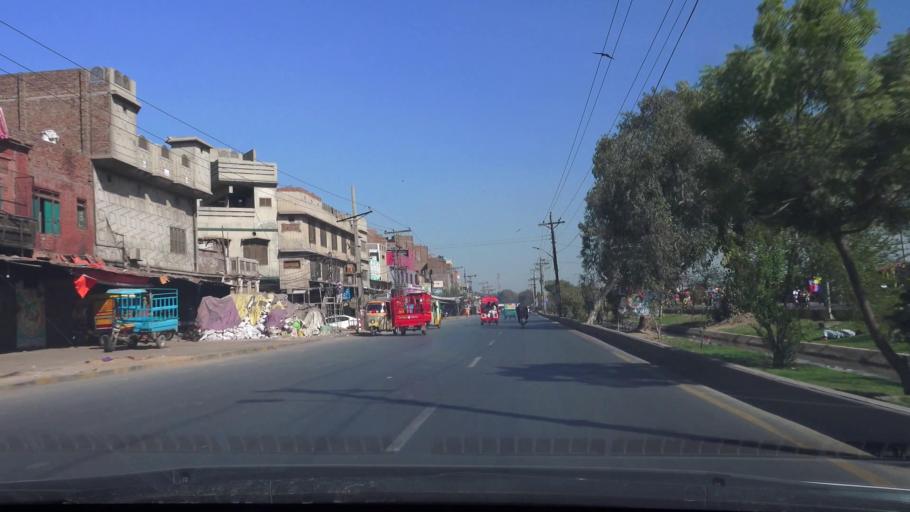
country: PK
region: Punjab
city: Faisalabad
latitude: 31.4142
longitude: 73.0745
